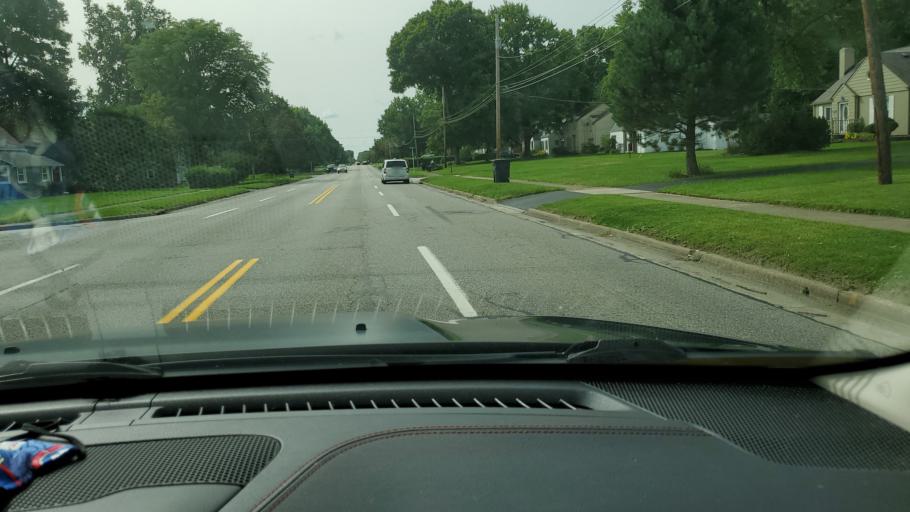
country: US
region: Ohio
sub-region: Mahoning County
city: Boardman
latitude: 41.0330
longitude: -80.6723
